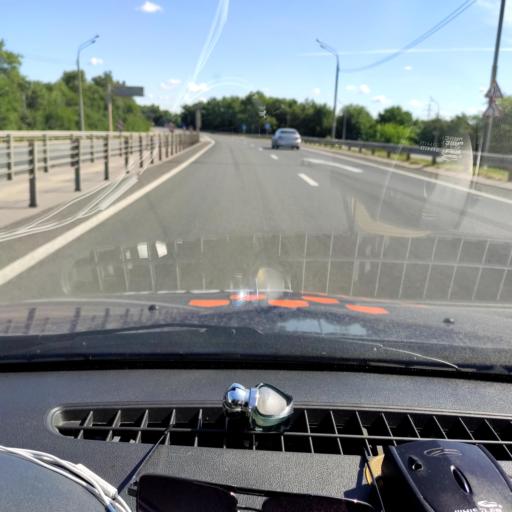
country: RU
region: Lipetsk
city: Khlevnoye
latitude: 52.2170
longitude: 39.1466
